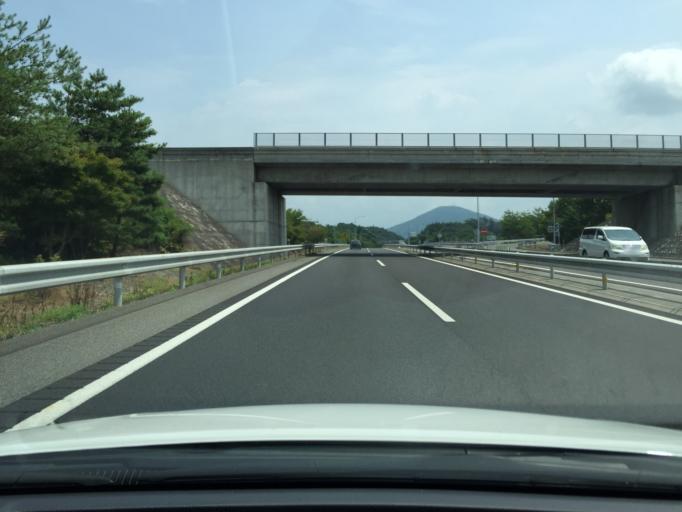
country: JP
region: Fukushima
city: Miharu
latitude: 37.4386
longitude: 140.5216
